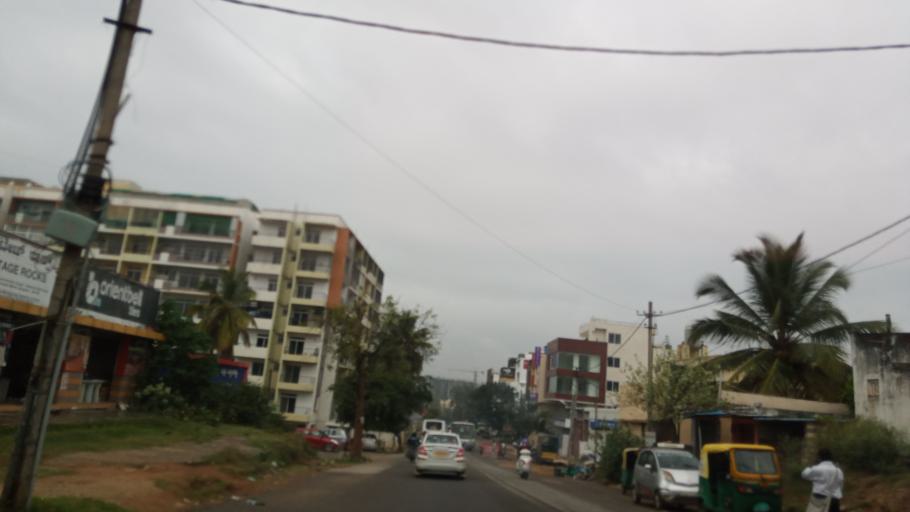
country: IN
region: Karnataka
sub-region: Bangalore Urban
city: Bangalore
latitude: 12.9035
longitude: 77.5158
